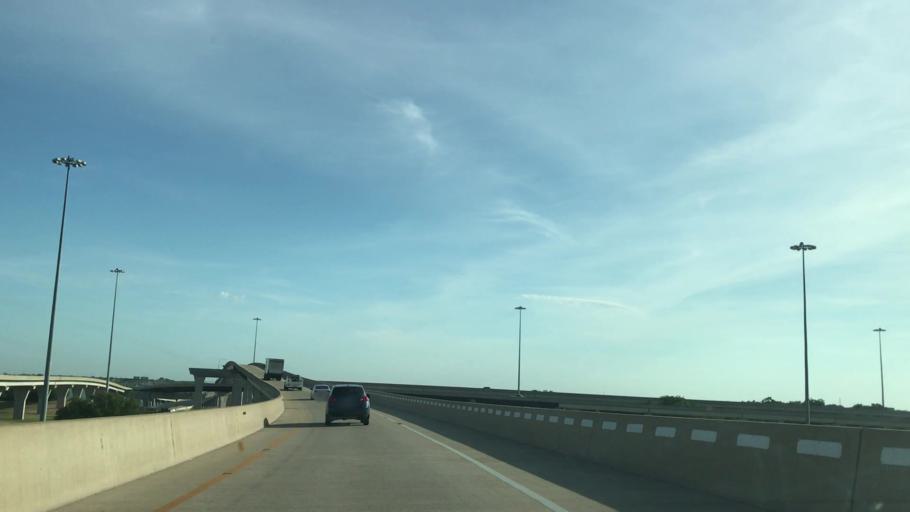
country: US
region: Texas
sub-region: Dallas County
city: Rowlett
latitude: 32.8574
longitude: -96.5562
